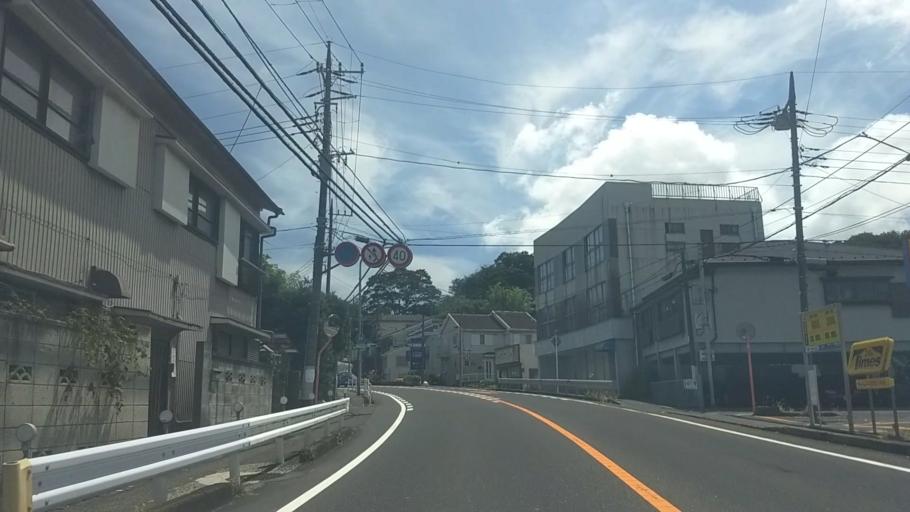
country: JP
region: Kanagawa
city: Yokosuka
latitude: 35.2540
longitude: 139.6654
